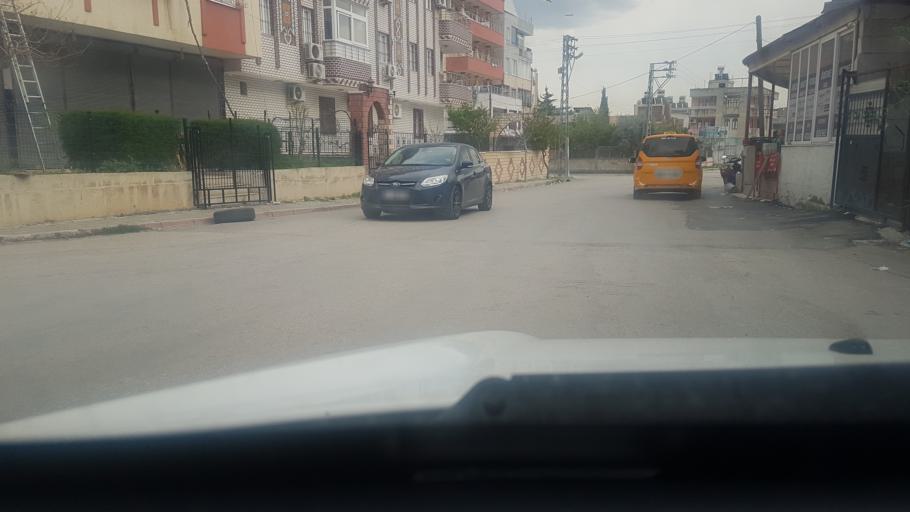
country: TR
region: Adana
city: Seyhan
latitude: 37.0191
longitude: 35.2765
